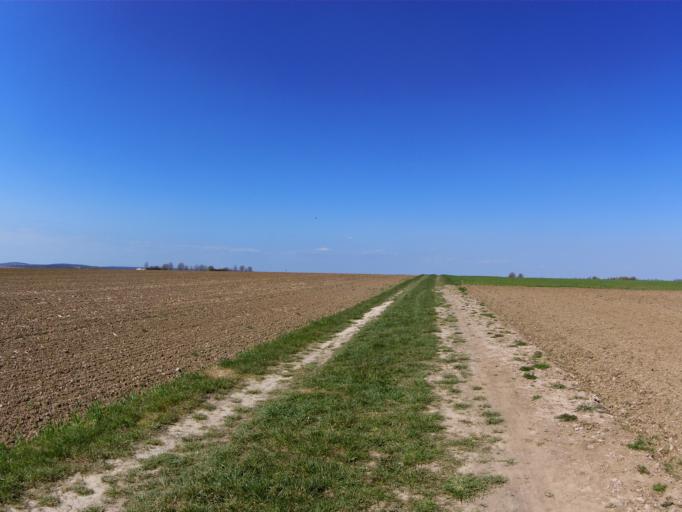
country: DE
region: Bavaria
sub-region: Regierungsbezirk Unterfranken
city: Kurnach
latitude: 49.8308
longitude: 10.0466
